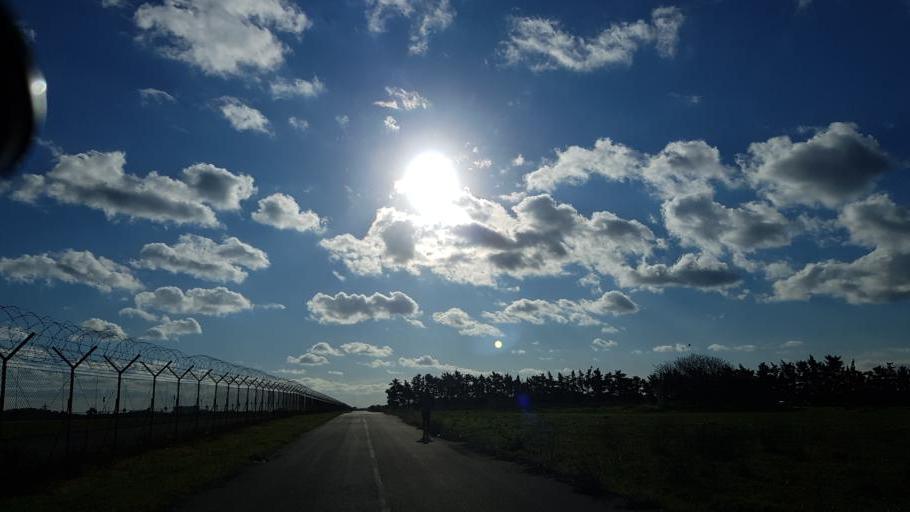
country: IT
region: Apulia
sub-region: Provincia di Brindisi
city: Materdomini
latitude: 40.6693
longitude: 17.9308
